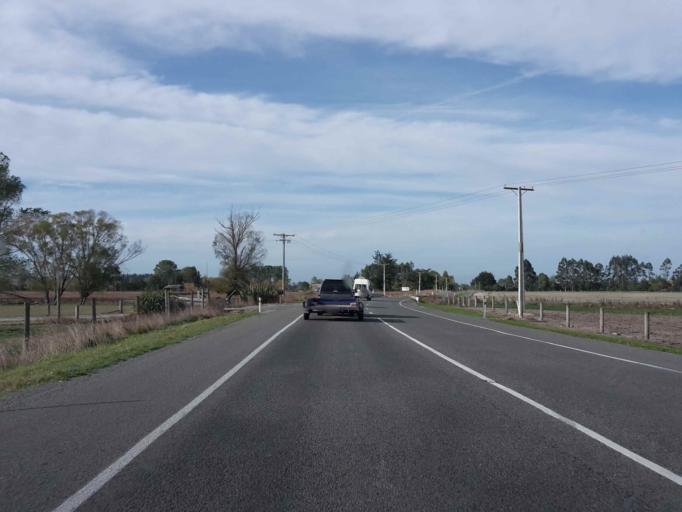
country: NZ
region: Canterbury
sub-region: Timaru District
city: Pleasant Point
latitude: -44.1195
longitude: 171.1985
